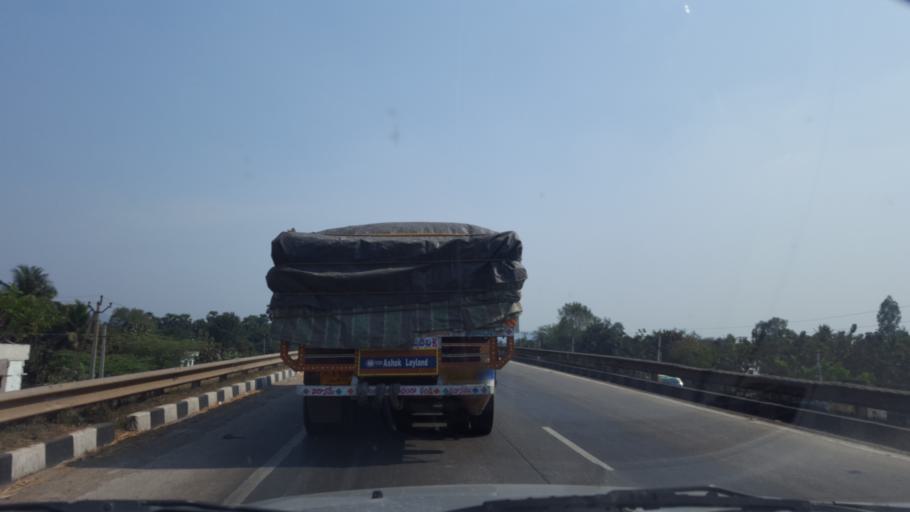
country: IN
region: Andhra Pradesh
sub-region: Vishakhapatnam
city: Anakapalle
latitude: 17.6810
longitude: 82.9896
